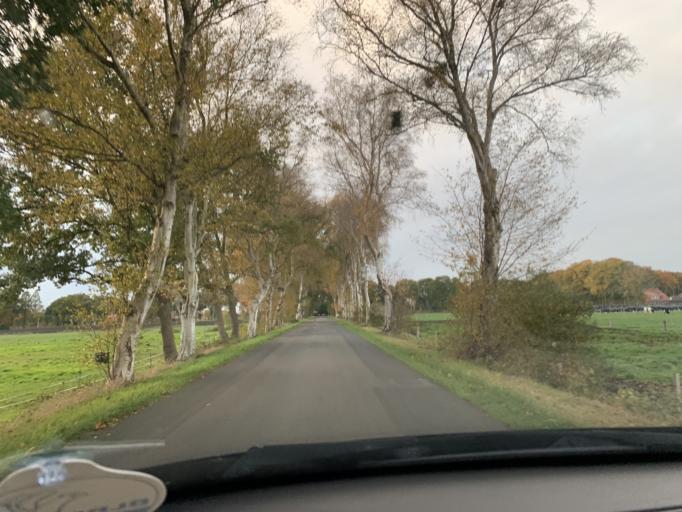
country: DE
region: Lower Saxony
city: Wiefelstede
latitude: 53.2684
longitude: 8.0802
